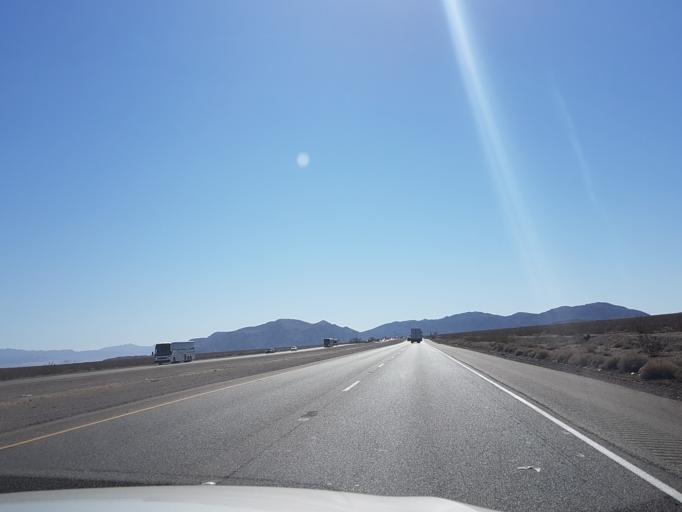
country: US
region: California
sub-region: San Bernardino County
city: Fort Irwin
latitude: 35.2383
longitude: -116.0987
